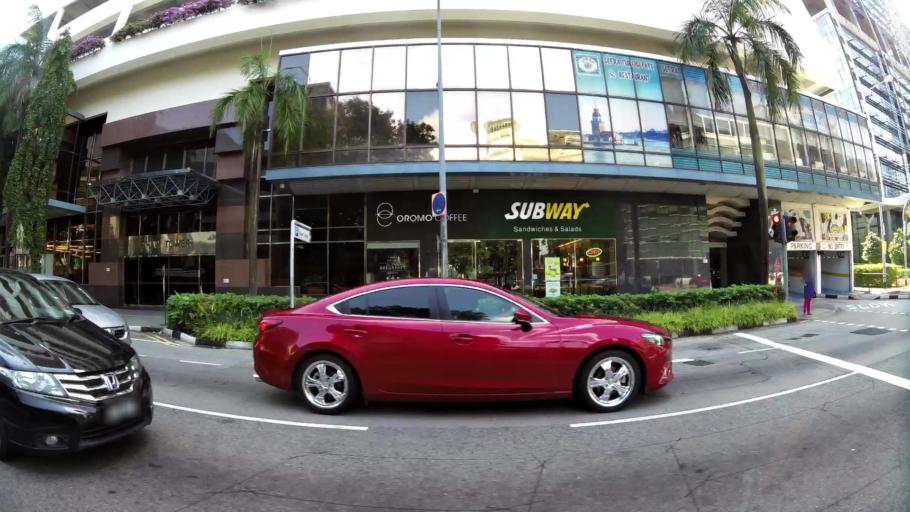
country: SG
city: Singapore
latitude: 1.2966
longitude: 103.8565
